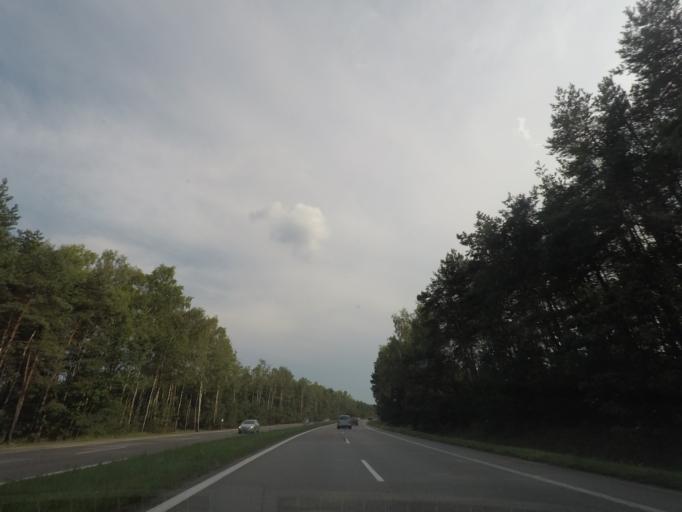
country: PL
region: Silesian Voivodeship
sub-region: Dabrowa Gornicza
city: Dabrowa Gornicza
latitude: 50.3676
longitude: 19.2502
